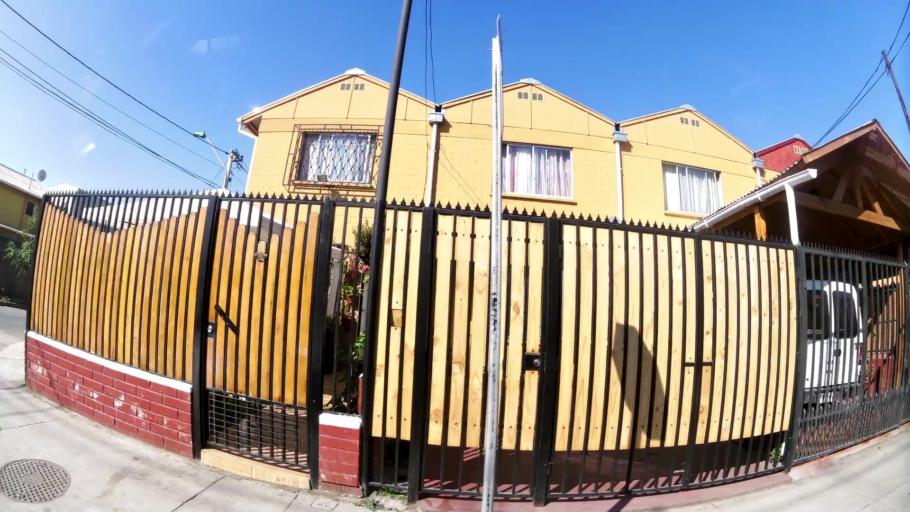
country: CL
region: Santiago Metropolitan
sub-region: Provincia de Santiago
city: La Pintana
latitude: -33.5638
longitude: -70.6202
